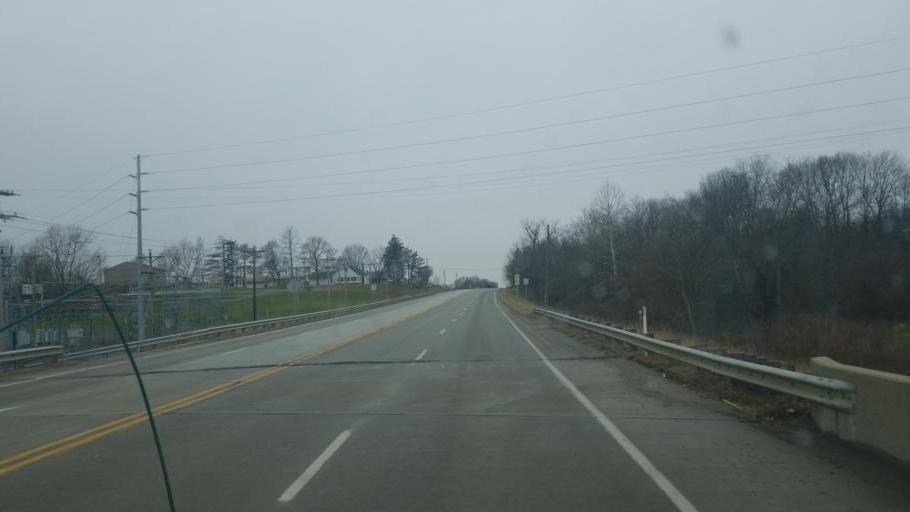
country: US
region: Indiana
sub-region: Henry County
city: Knightstown
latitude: 39.7945
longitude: -85.5365
